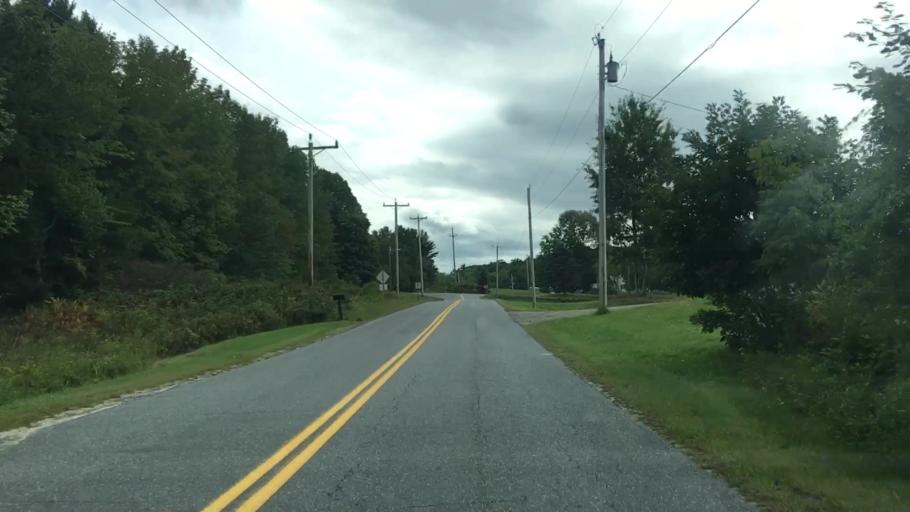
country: US
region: Maine
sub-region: Kennebec County
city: Hallowell
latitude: 44.2665
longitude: -69.8139
